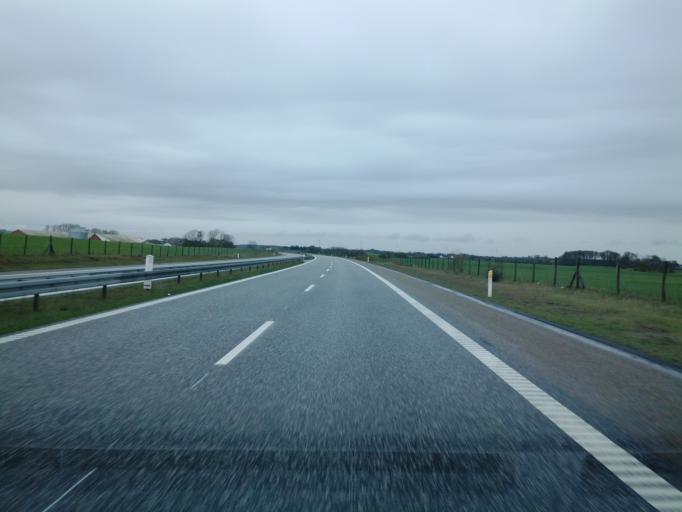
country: DK
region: North Denmark
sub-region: Frederikshavn Kommune
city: Saeby
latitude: 57.2919
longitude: 10.4211
